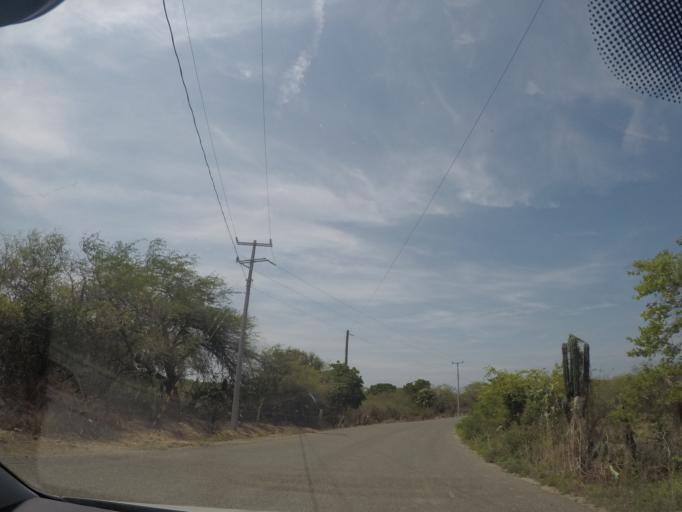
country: MX
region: Oaxaca
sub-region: Salina Cruz
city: Salina Cruz
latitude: 16.2009
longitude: -95.1198
